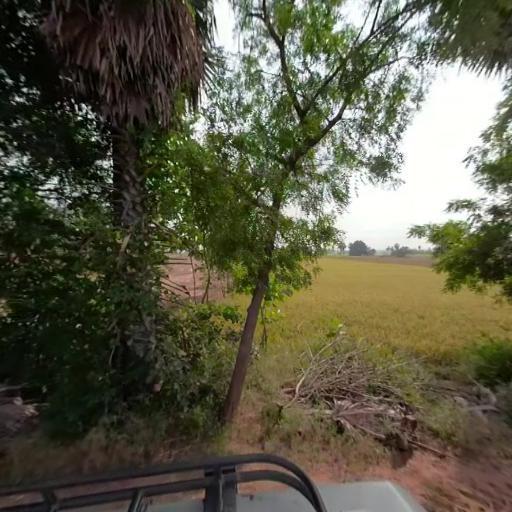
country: IN
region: Telangana
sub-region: Nalgonda
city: Suriapet
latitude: 17.2082
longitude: 79.4943
